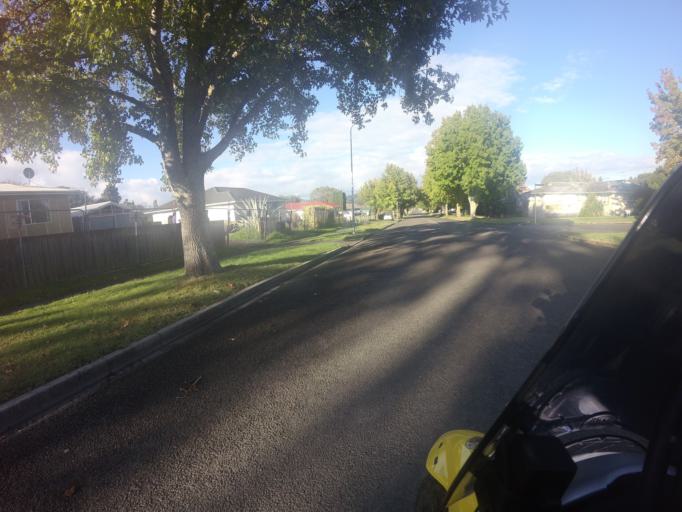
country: NZ
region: Gisborne
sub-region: Gisborne District
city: Gisborne
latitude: -38.6670
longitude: 178.0570
